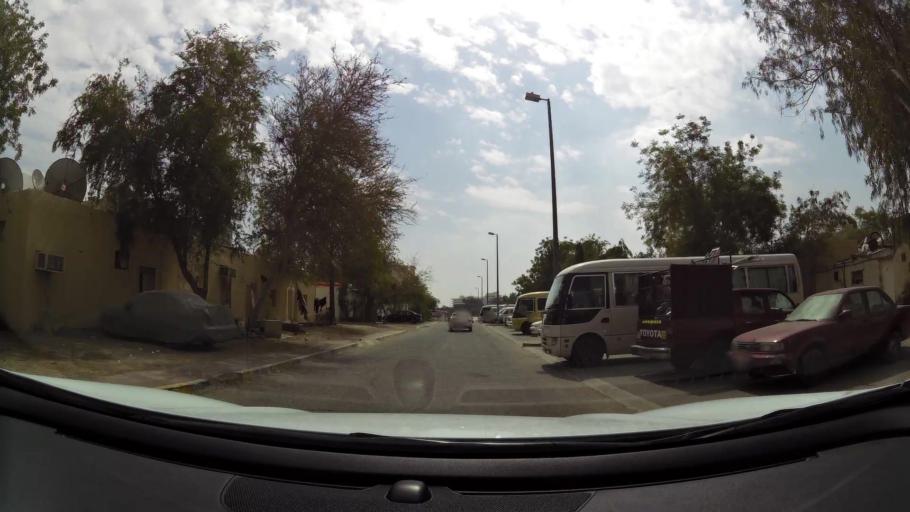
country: AE
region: Abu Dhabi
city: Al Ain
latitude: 24.2127
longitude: 55.7825
